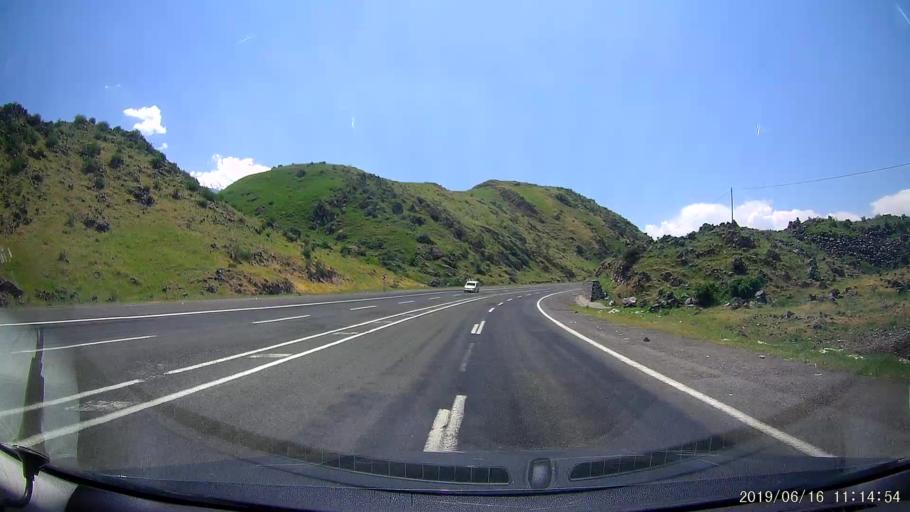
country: TR
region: Igdir
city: Igdir
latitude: 39.7719
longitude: 44.1430
